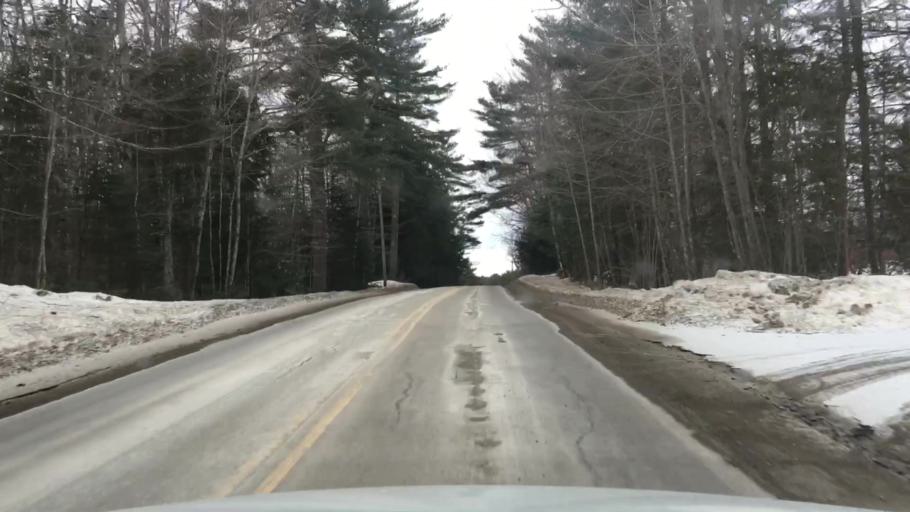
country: US
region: Maine
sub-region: Lincoln County
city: Whitefield
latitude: 44.2392
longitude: -69.6241
